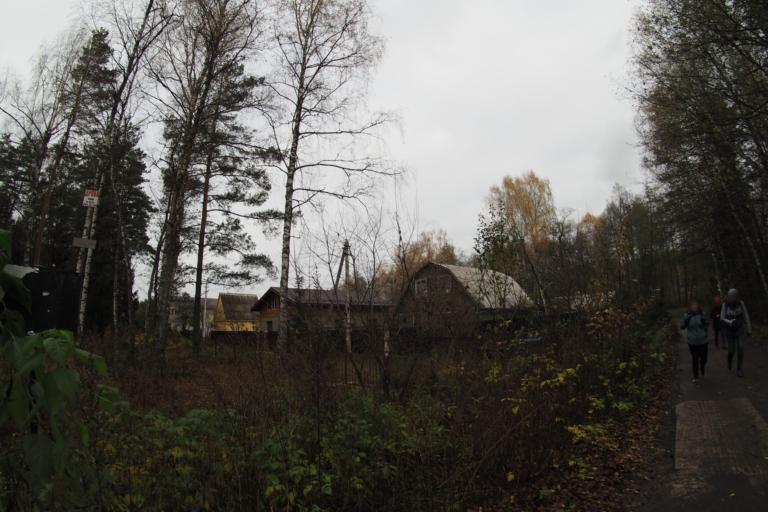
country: RU
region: Moskovskaya
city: Davydovo
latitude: 55.5754
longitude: 38.7585
